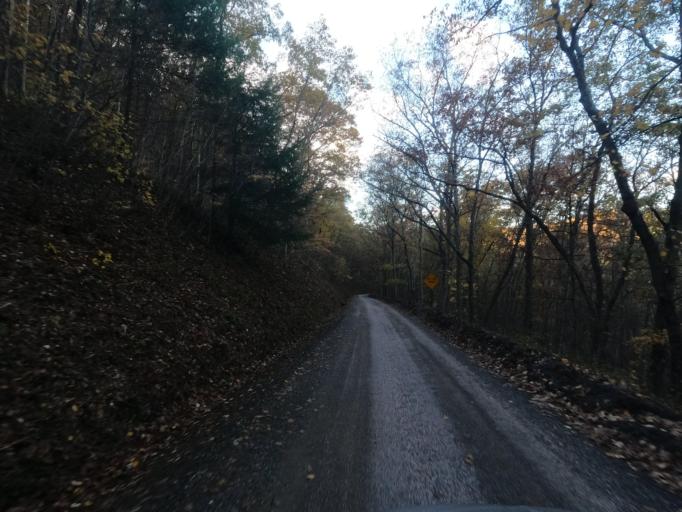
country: US
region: West Virginia
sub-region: Morgan County
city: Berkeley Springs
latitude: 39.6594
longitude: -78.4608
